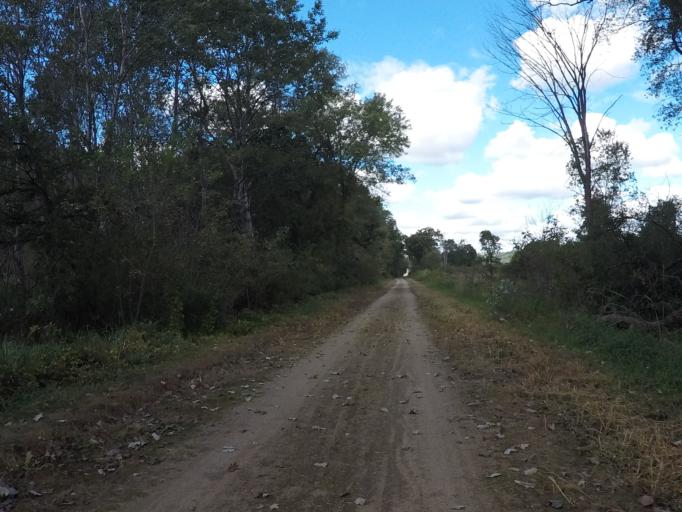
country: US
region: Wisconsin
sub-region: Richland County
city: Richland Center
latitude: 43.3040
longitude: -90.3394
